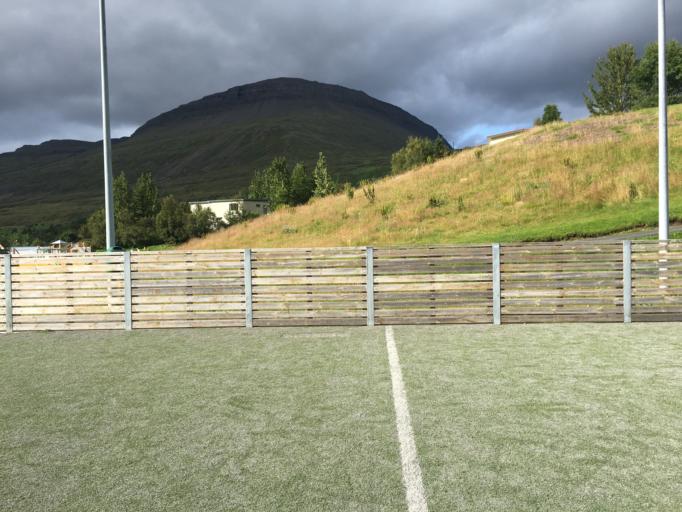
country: IS
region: East
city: Reydarfjoerdur
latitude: 65.0349
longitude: -14.2104
